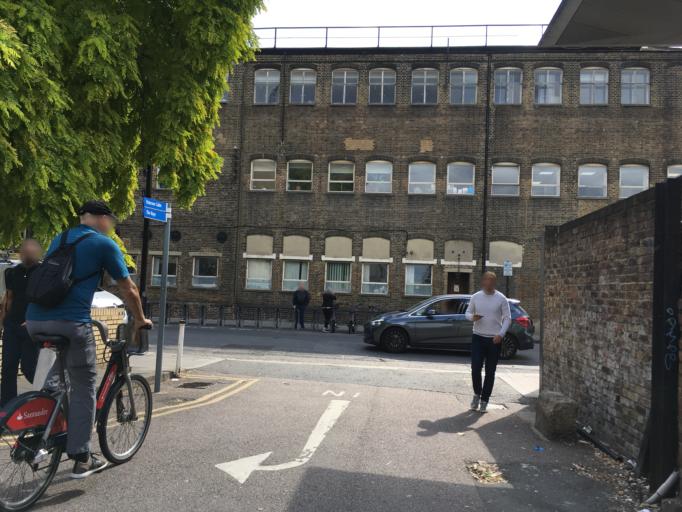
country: GB
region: England
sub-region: Greater London
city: Bayswater
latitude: 51.5174
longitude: -0.1761
